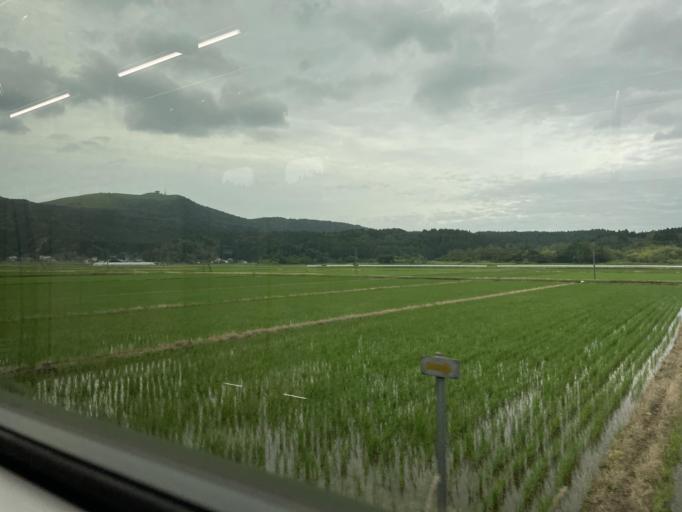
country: JP
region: Akita
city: Tenno
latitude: 39.9165
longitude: 139.8958
